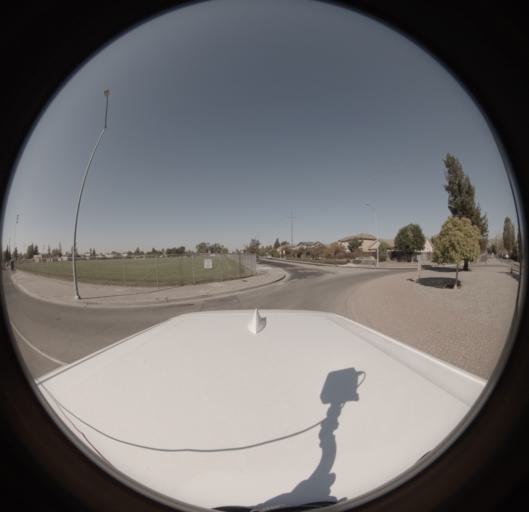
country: US
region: California
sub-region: Sonoma County
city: Petaluma
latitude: 38.2433
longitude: -122.5959
